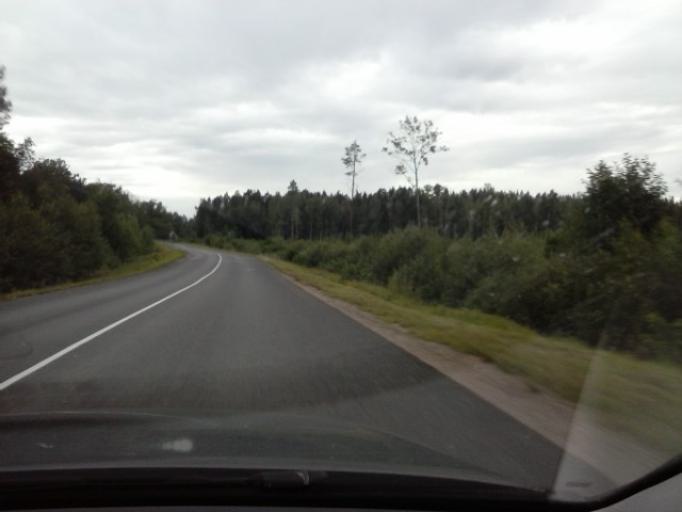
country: LV
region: Kuldigas Rajons
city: Kuldiga
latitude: 56.8952
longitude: 22.0900
